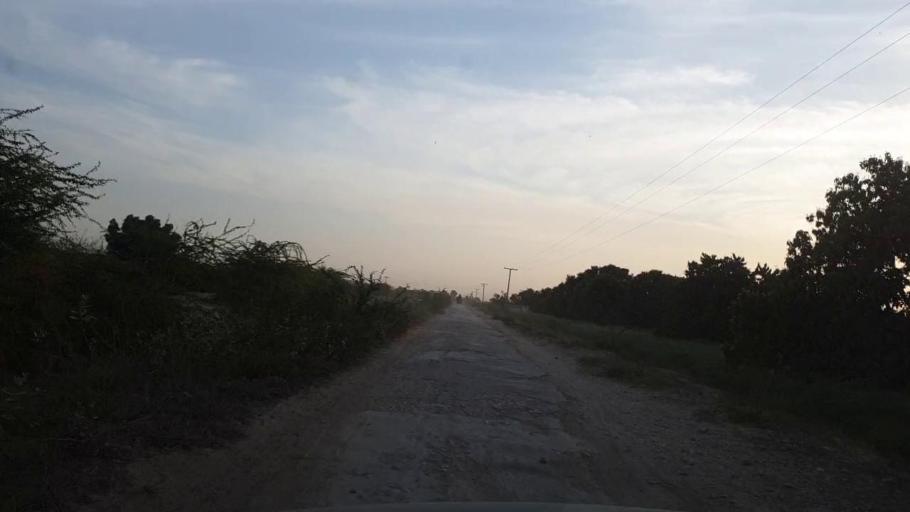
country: PK
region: Sindh
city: Kunri
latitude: 25.1478
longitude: 69.5823
